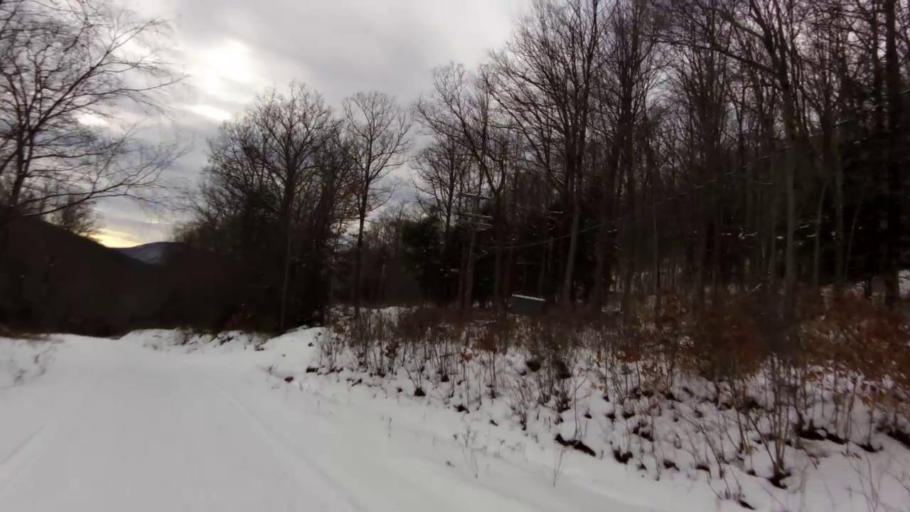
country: US
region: Pennsylvania
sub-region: McKean County
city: Foster Brook
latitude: 42.0079
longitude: -78.6008
